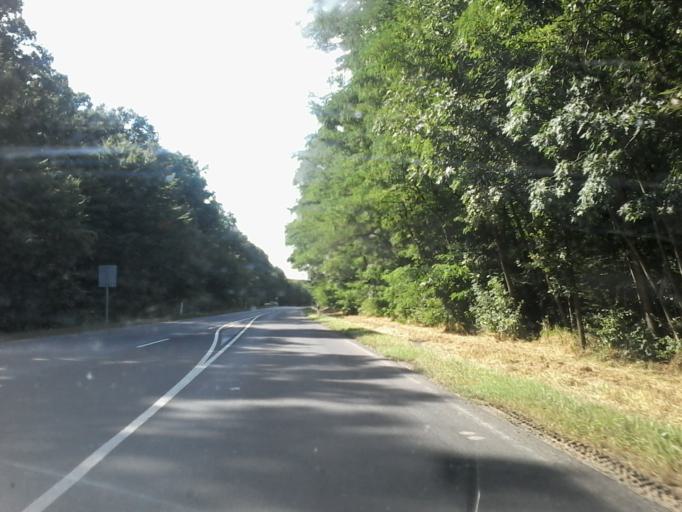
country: HU
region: Vas
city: Janoshaza
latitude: 47.1025
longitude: 17.1531
